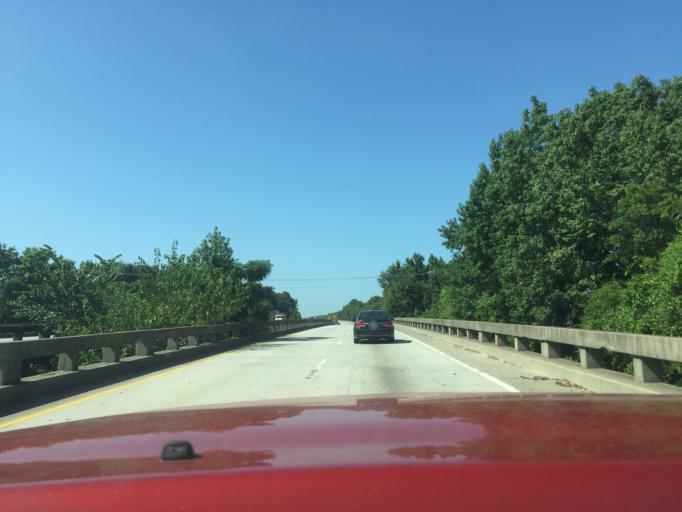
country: US
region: Georgia
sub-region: Chatham County
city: Savannah
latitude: 32.0847
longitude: -81.1299
